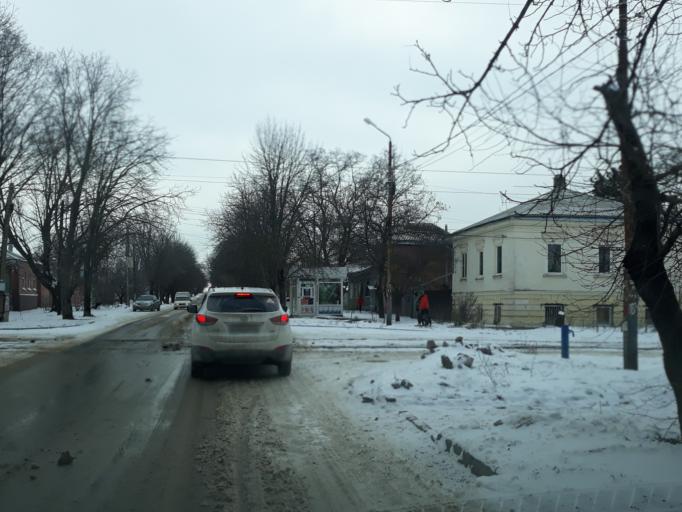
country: RU
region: Rostov
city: Taganrog
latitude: 47.2060
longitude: 38.9209
